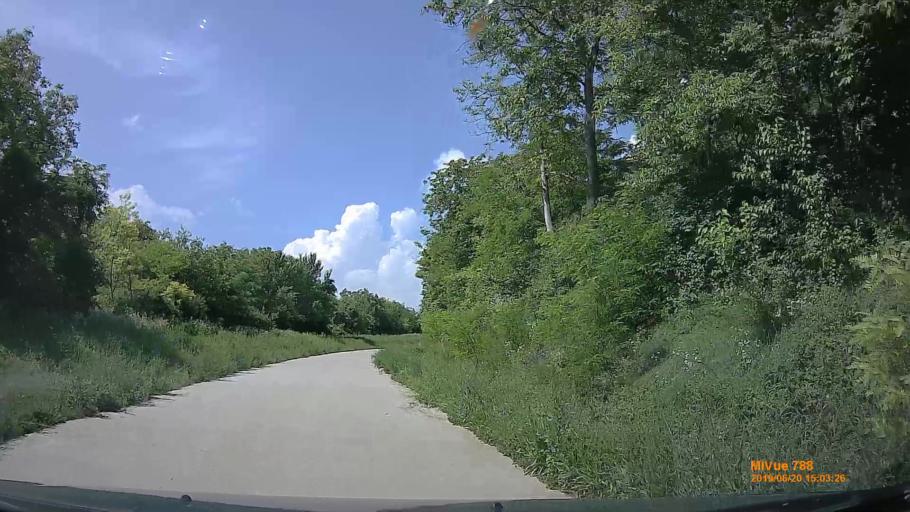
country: HU
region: Baranya
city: Kozarmisleny
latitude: 45.9877
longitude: 18.2618
